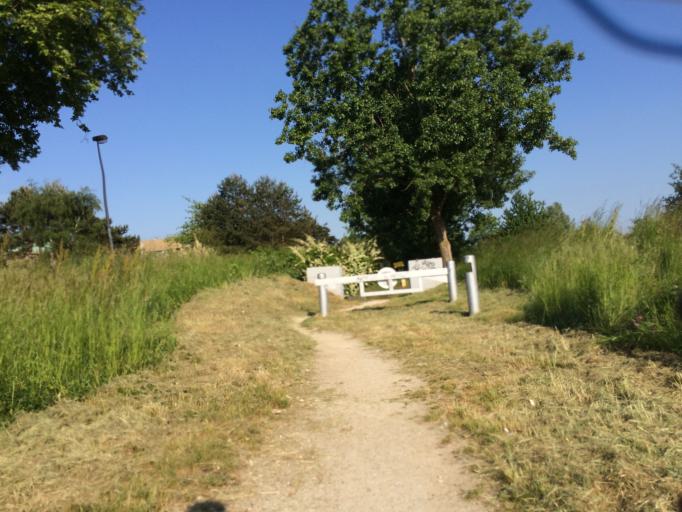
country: FR
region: Ile-de-France
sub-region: Departement de l'Essonne
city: Bondoufle
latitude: 48.6189
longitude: 2.3836
